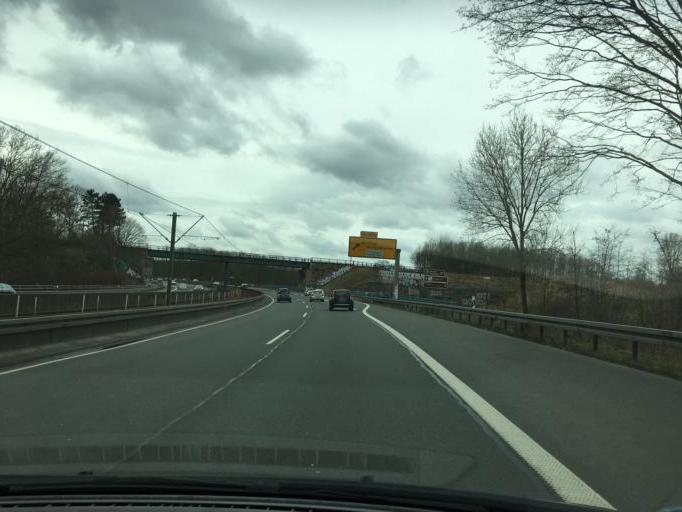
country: DE
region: North Rhine-Westphalia
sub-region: Regierungsbezirk Arnsberg
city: Dortmund
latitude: 51.4881
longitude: 7.4671
